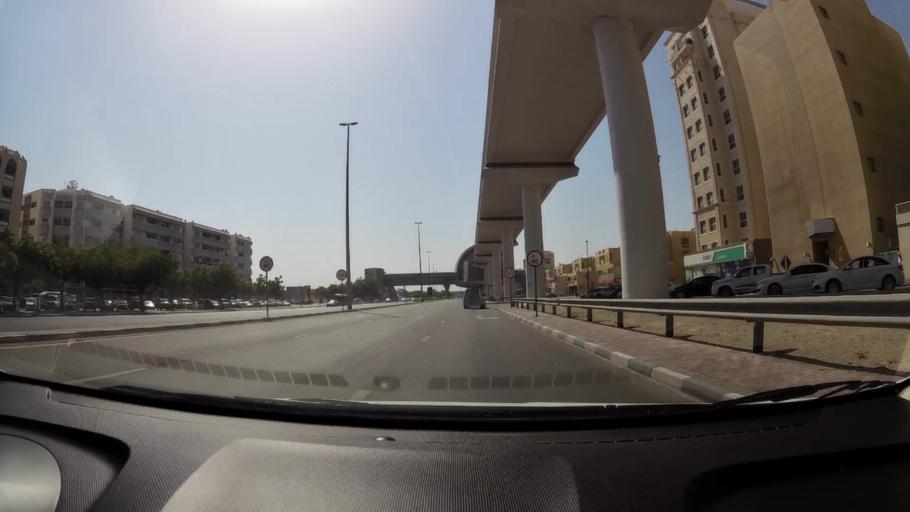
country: AE
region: Ash Shariqah
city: Sharjah
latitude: 25.2687
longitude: 55.3772
